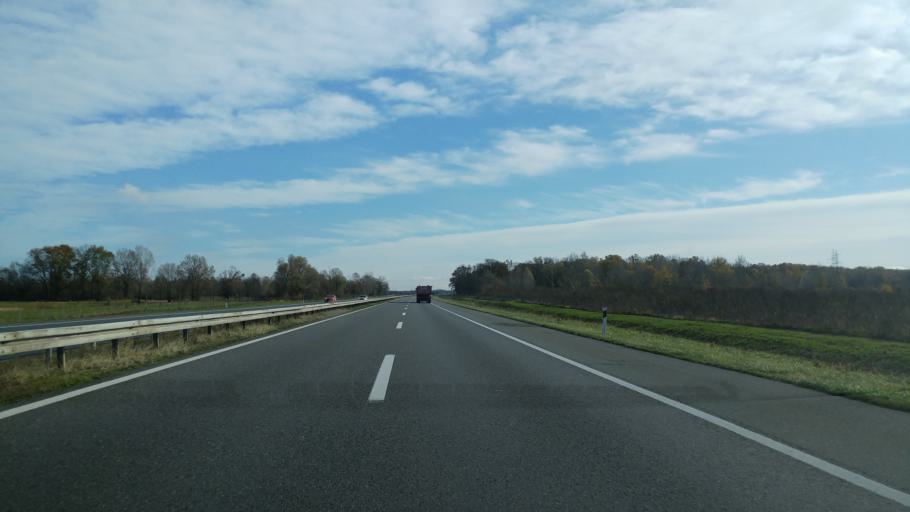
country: HR
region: Sisacko-Moslavacka
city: Repusnica
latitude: 45.4765
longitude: 16.7295
